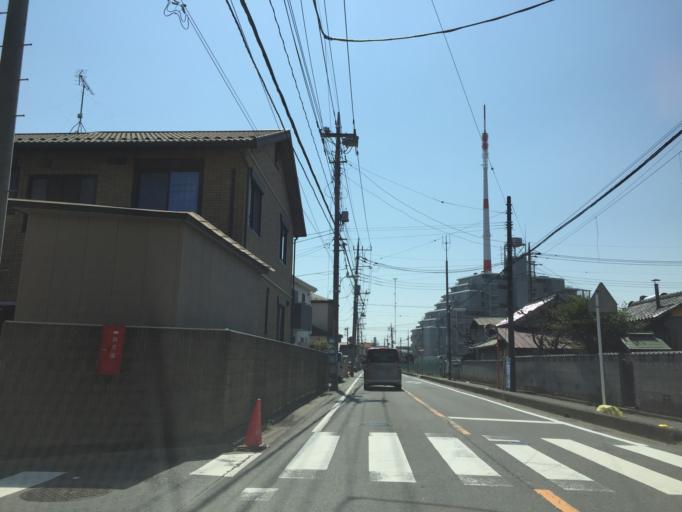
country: JP
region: Saitama
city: Yono
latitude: 35.8561
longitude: 139.6151
